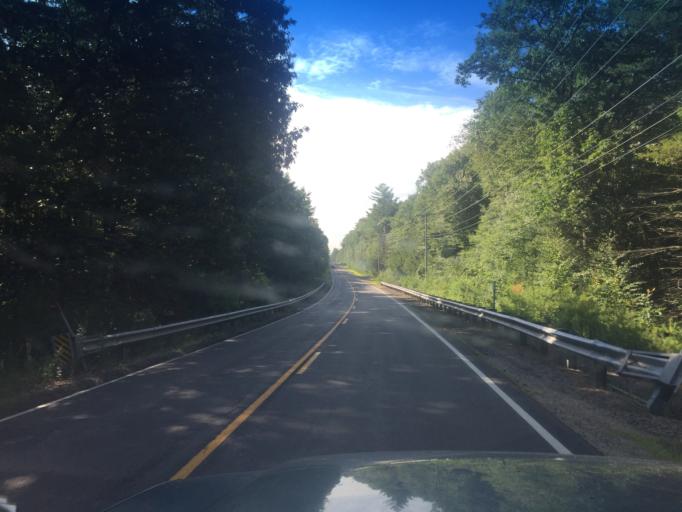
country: US
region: Maine
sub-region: York County
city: Eliot
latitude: 43.1949
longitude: -70.7542
